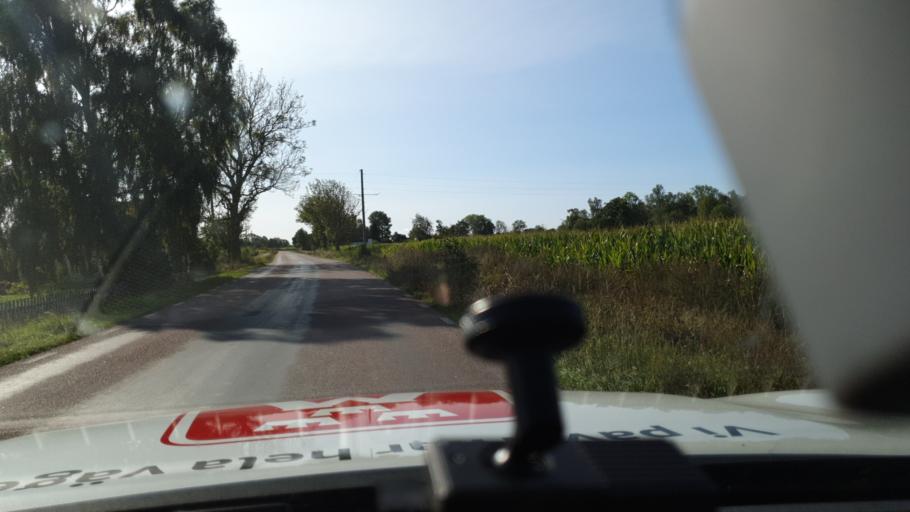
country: SE
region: Gotland
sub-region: Gotland
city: Hemse
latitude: 57.1579
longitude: 18.2809
